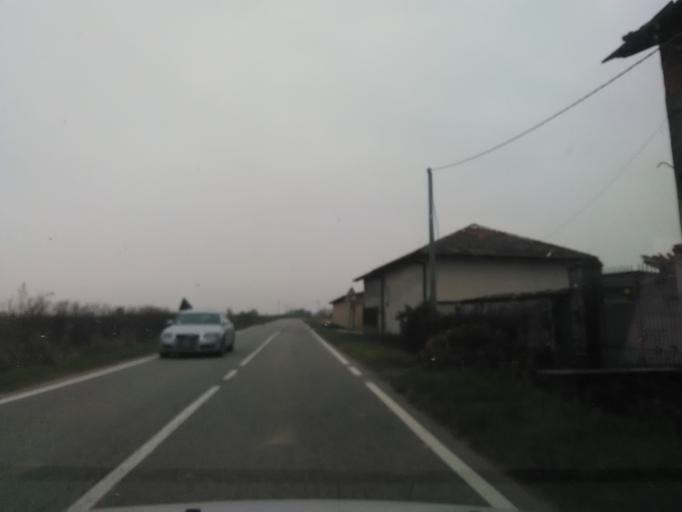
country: IT
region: Piedmont
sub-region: Provincia di Vercelli
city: Bianze
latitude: 45.2795
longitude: 8.1090
